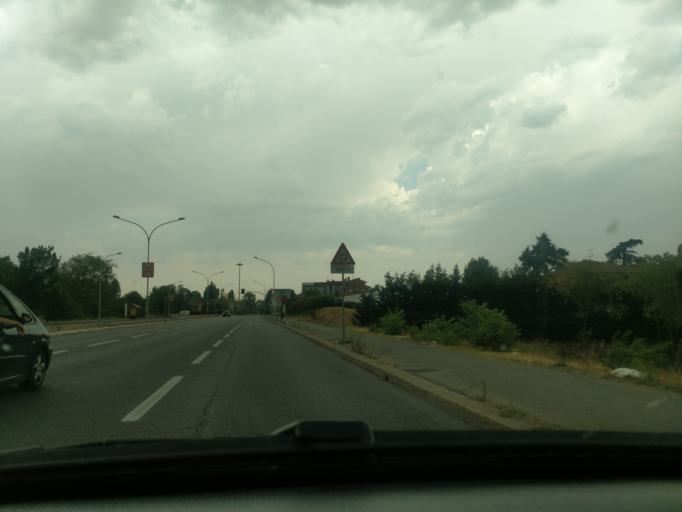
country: IT
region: Emilia-Romagna
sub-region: Provincia di Bologna
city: Casalecchio di Reno
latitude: 44.5065
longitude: 11.2858
